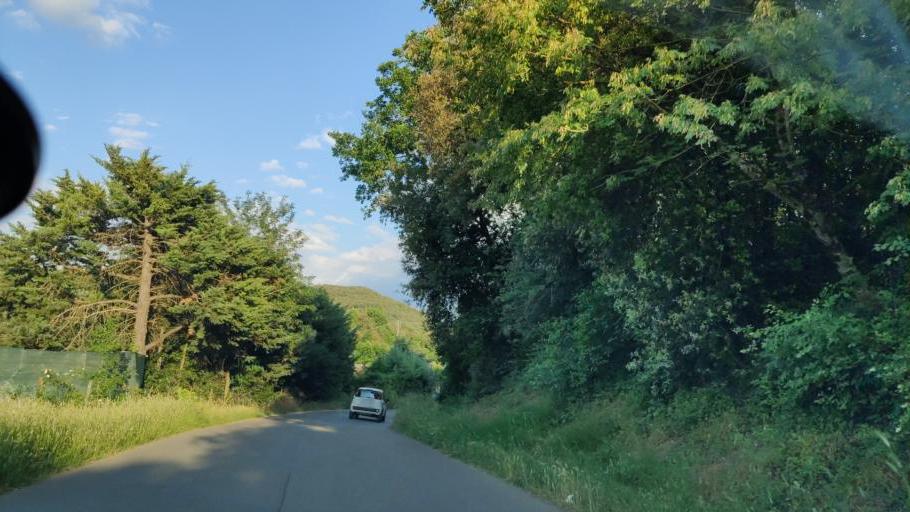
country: IT
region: Umbria
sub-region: Provincia di Terni
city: Amelia
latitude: 42.5705
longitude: 12.4050
